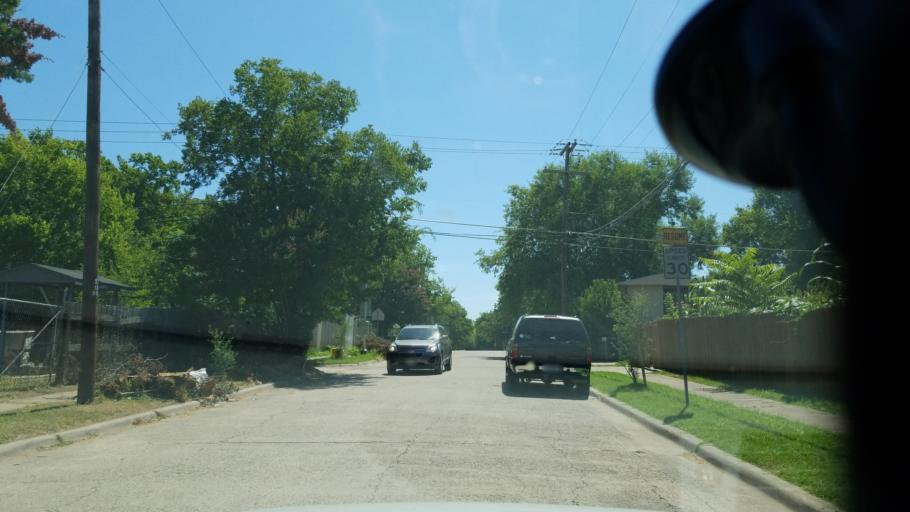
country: US
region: Texas
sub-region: Dallas County
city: Cockrell Hill
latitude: 32.7075
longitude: -96.8227
